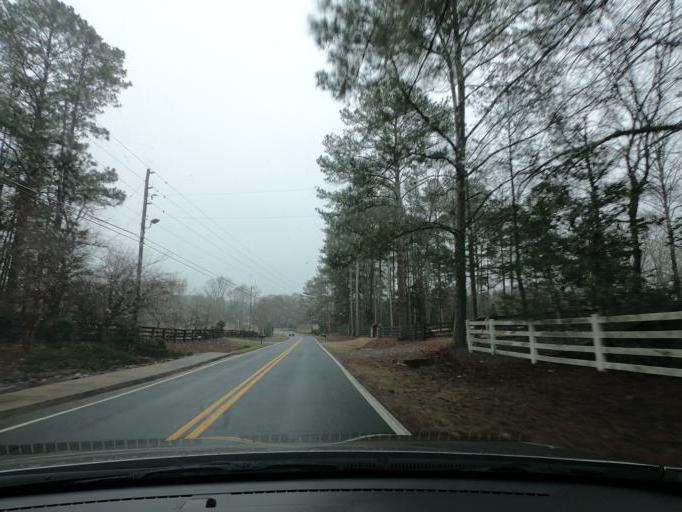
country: US
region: Georgia
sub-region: Fulton County
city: Milton
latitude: 34.1393
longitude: -84.2779
